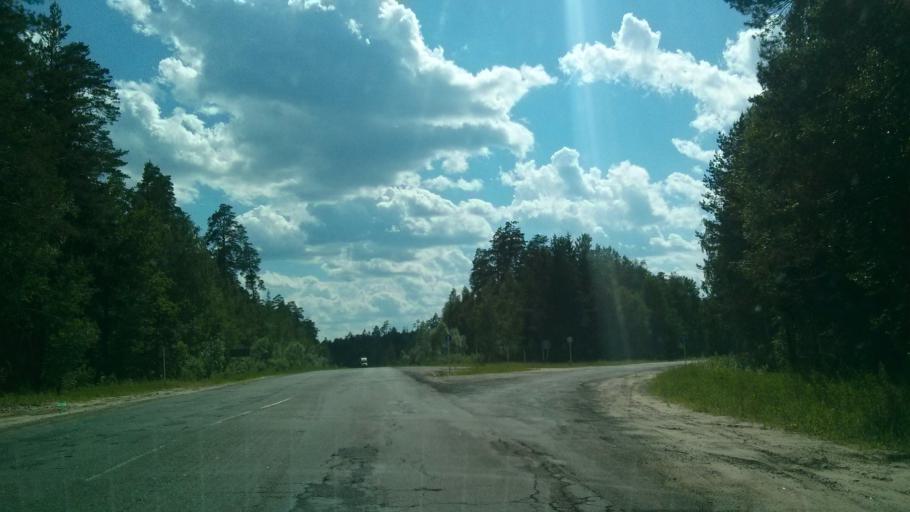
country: RU
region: Vladimir
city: Melenki
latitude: 55.3542
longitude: 41.6811
